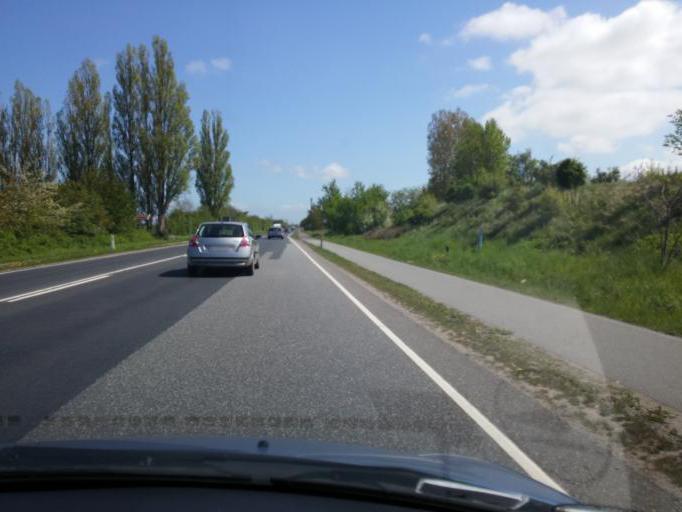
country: DK
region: South Denmark
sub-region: Odense Kommune
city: Bullerup
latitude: 55.4274
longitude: 10.4622
